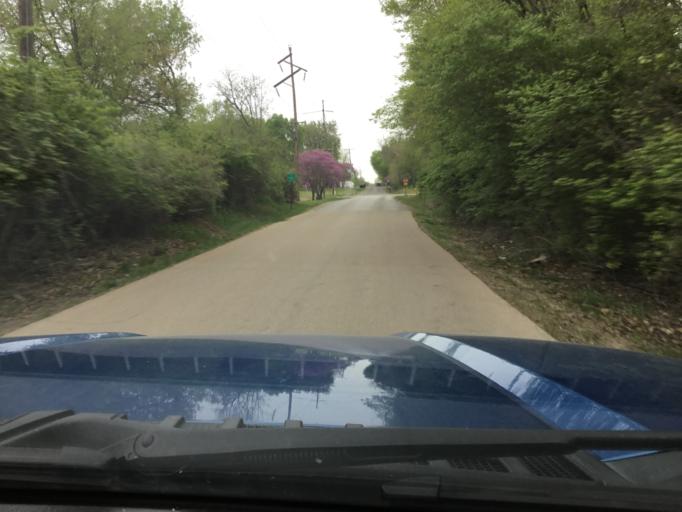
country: US
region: Kansas
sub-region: Shawnee County
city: Topeka
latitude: 39.1083
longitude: -95.6874
